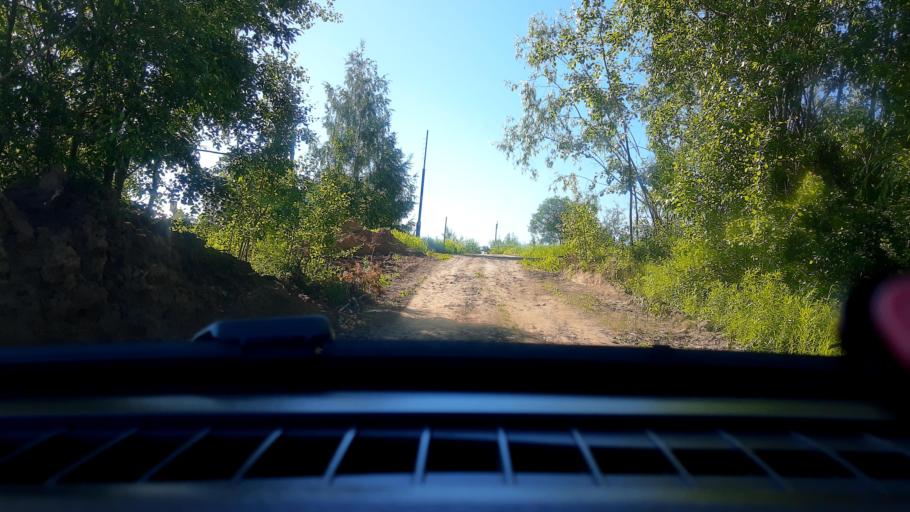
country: RU
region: Nizjnij Novgorod
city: Afonino
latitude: 56.2565
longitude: 44.0521
